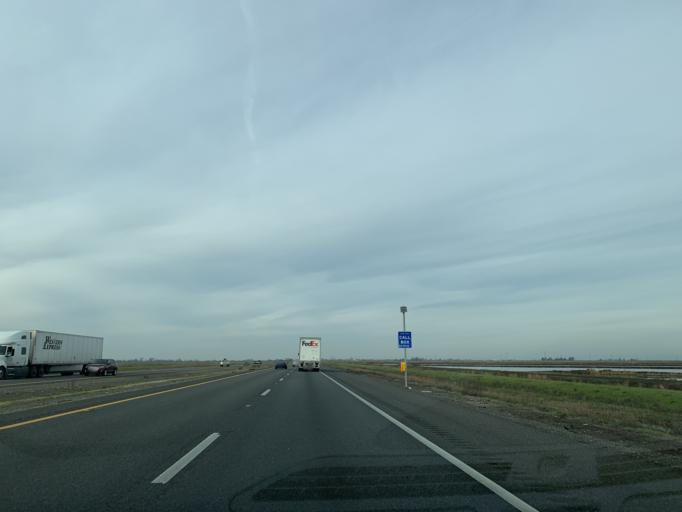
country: US
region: California
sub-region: Sacramento County
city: Elverta
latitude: 38.7936
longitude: -121.5436
